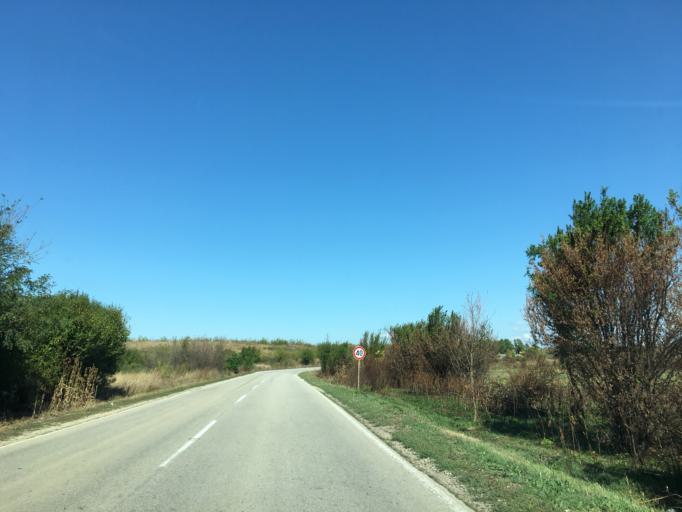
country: BG
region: Montana
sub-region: Obshtina Brusartsi
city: Brusartsi
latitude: 43.7069
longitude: 23.0088
